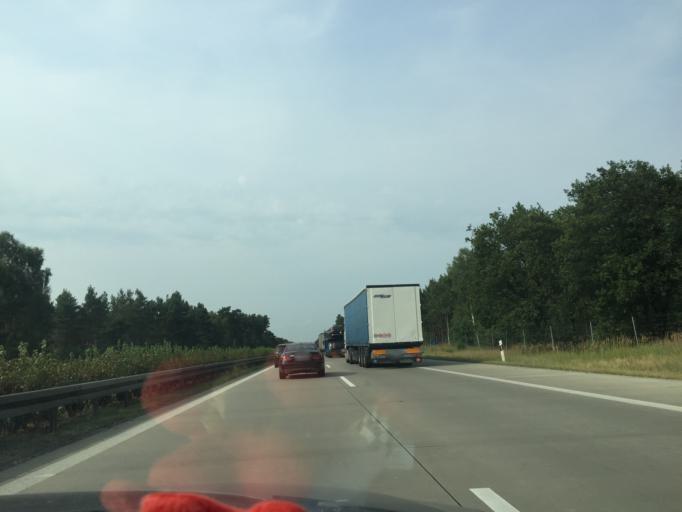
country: DE
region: Brandenburg
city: Halbe
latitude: 52.0666
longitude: 13.6522
